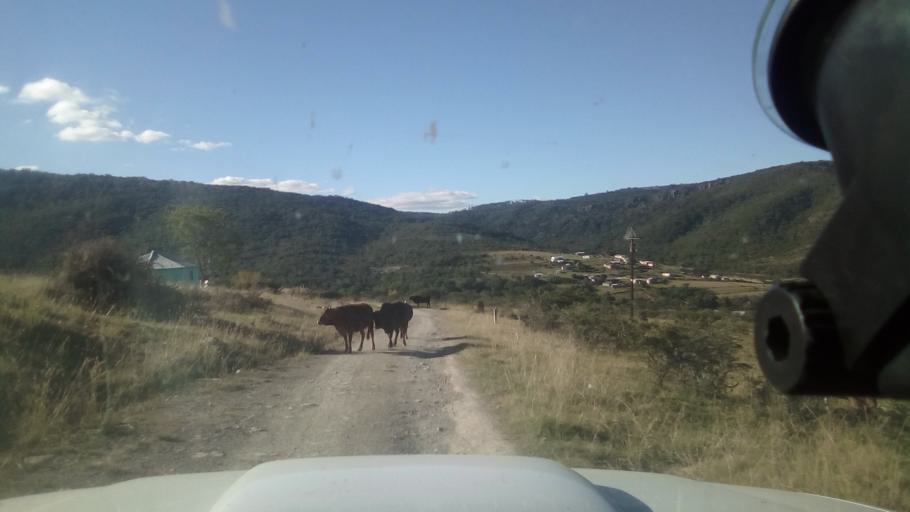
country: ZA
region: Eastern Cape
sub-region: Buffalo City Metropolitan Municipality
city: Bhisho
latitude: -32.7315
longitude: 27.3477
